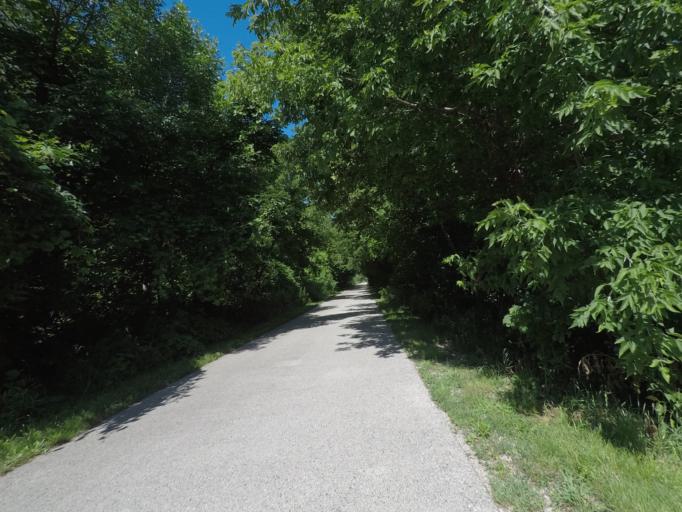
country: US
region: Wisconsin
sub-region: Milwaukee County
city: West Allis
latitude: 43.0243
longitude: -87.9914
